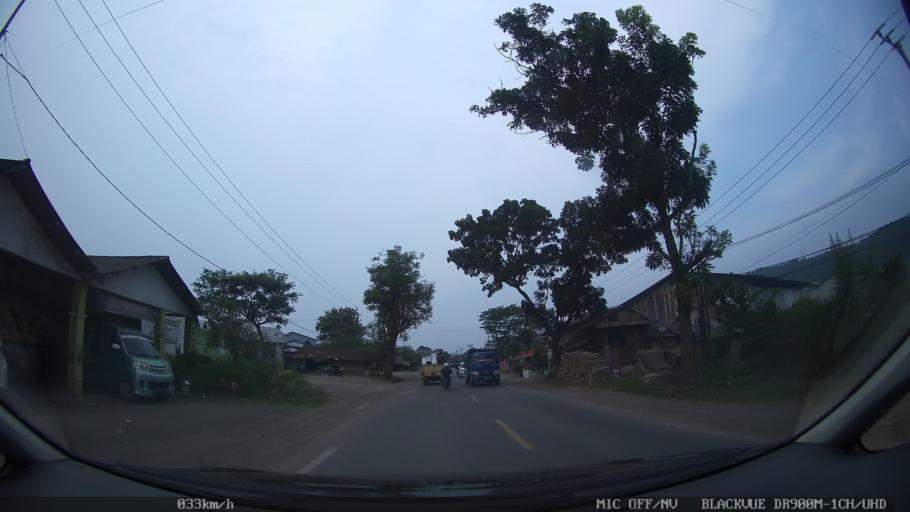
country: ID
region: Lampung
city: Panjang
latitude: -5.4275
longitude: 105.3285
